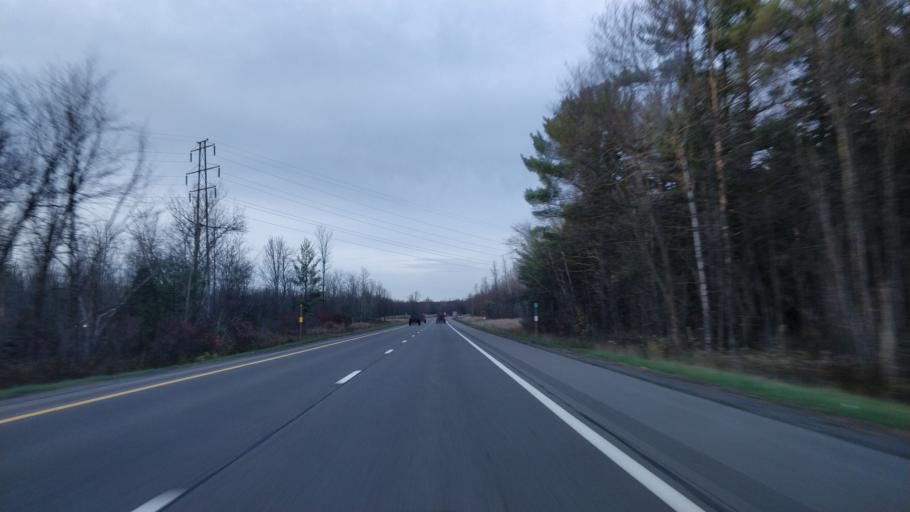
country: US
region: New York
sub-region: Oswego County
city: Central Square
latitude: 43.3397
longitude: -76.1225
